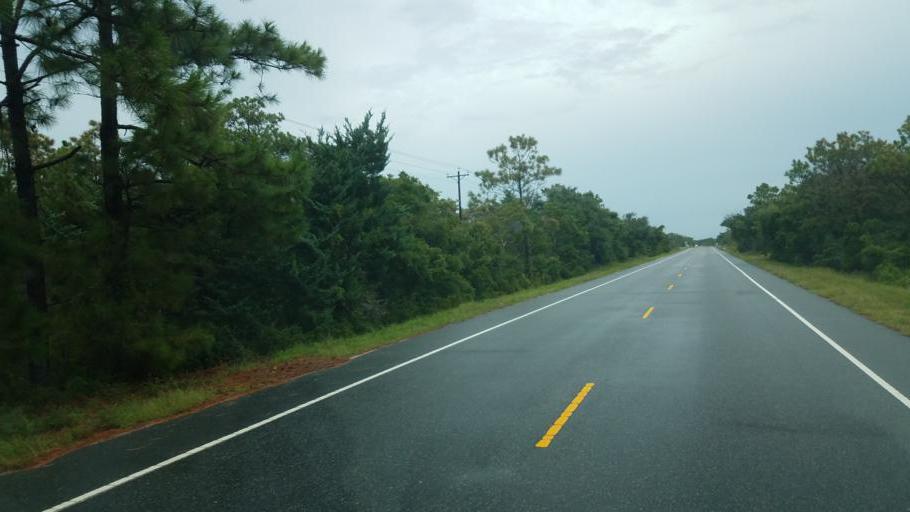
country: US
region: North Carolina
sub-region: Dare County
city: Buxton
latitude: 35.1329
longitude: -75.9116
